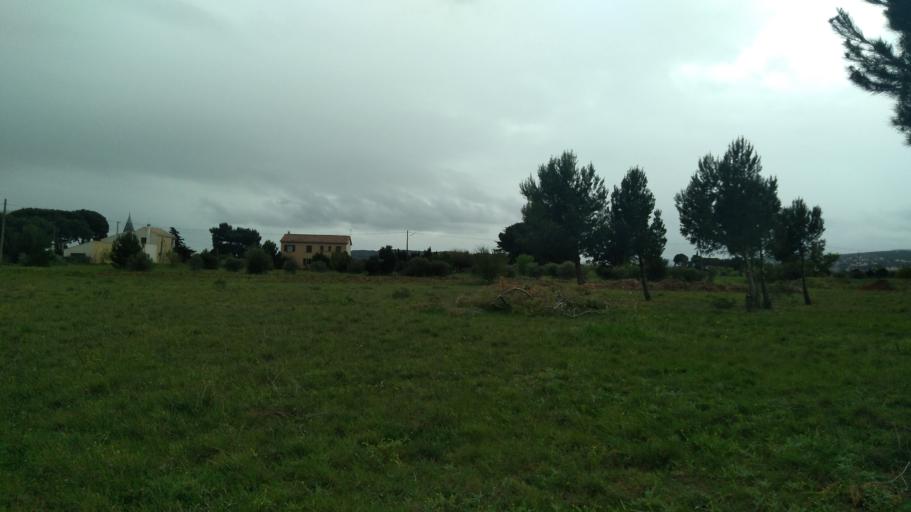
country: FR
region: Languedoc-Roussillon
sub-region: Departement de l'Aude
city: Narbonne
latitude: 43.1568
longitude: 2.9937
